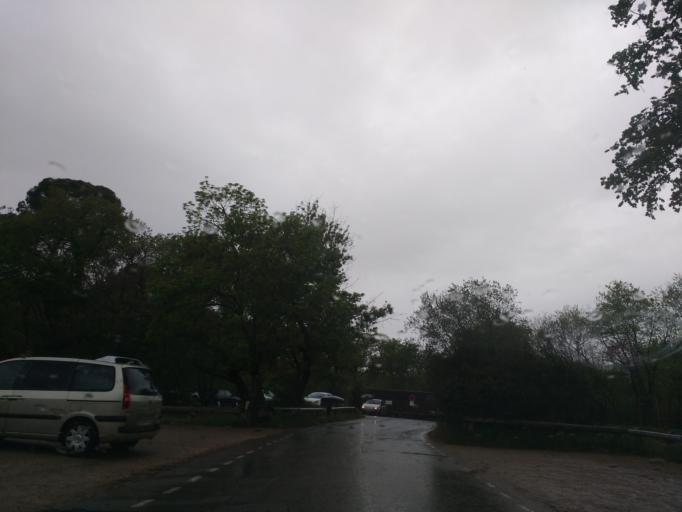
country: FR
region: Provence-Alpes-Cote d'Azur
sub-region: Departement des Alpes-Maritimes
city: Biot
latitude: 43.6253
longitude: 7.1288
